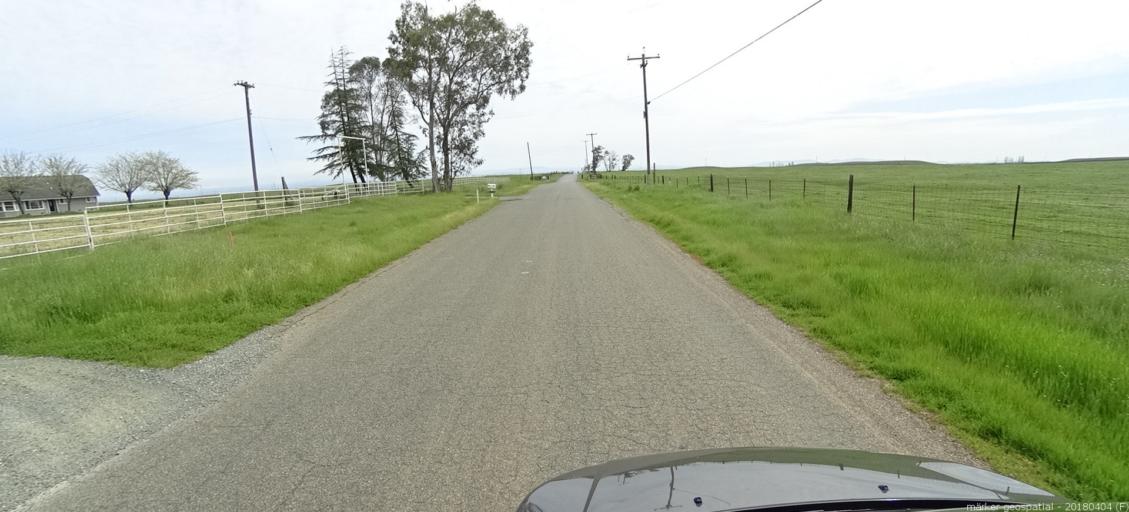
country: US
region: California
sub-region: Sacramento County
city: Clay
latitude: 38.2930
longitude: -121.1546
